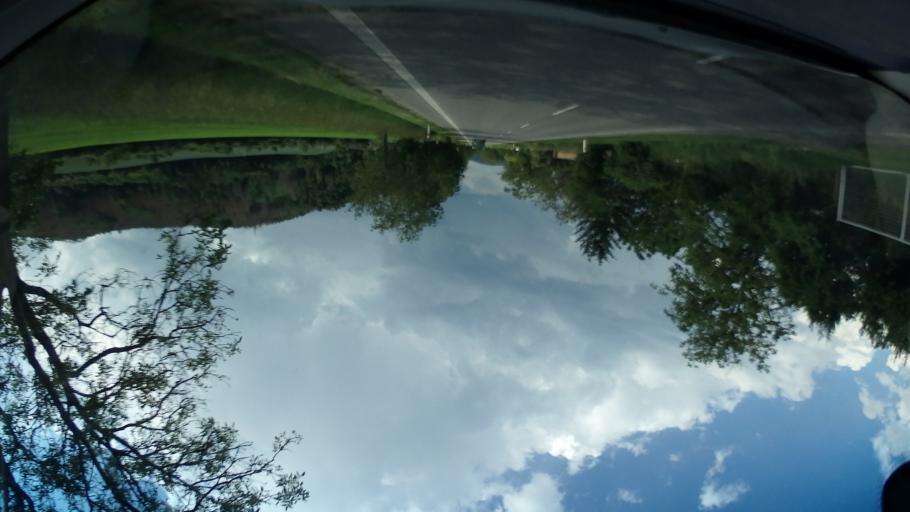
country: CZ
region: South Moravian
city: Predklasteri
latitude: 49.3499
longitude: 16.4093
